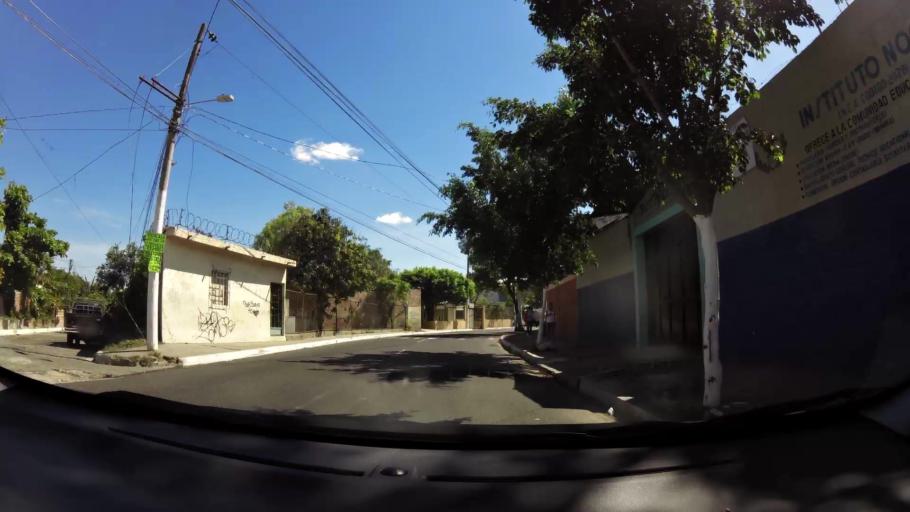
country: SV
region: San Salvador
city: Apopa
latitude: 13.8053
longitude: -89.1798
